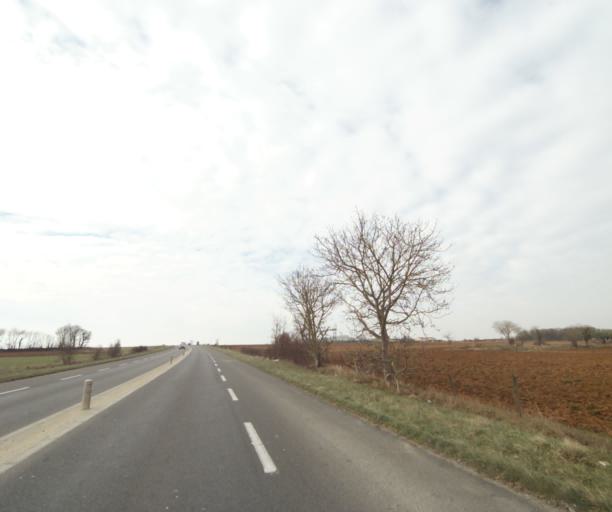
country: FR
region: Poitou-Charentes
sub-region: Departement des Deux-Sevres
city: Aiffres
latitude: 46.3112
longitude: -0.4263
